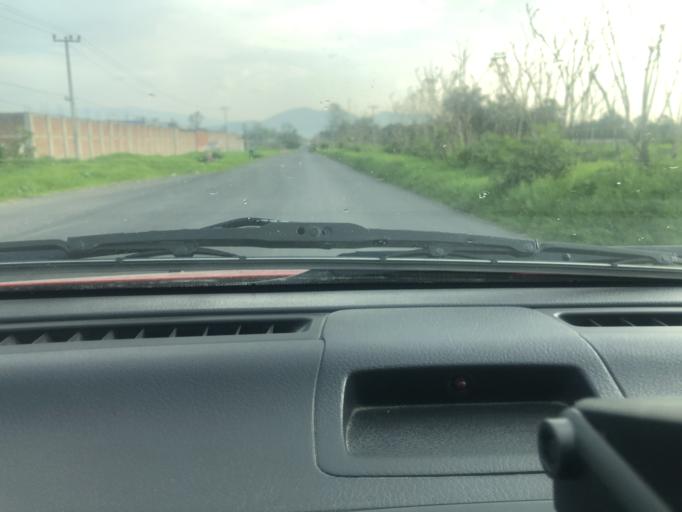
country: MX
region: Jalisco
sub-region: San Pedro Tlaquepaque
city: Paseo del Prado
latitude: 20.5735
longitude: -103.4055
